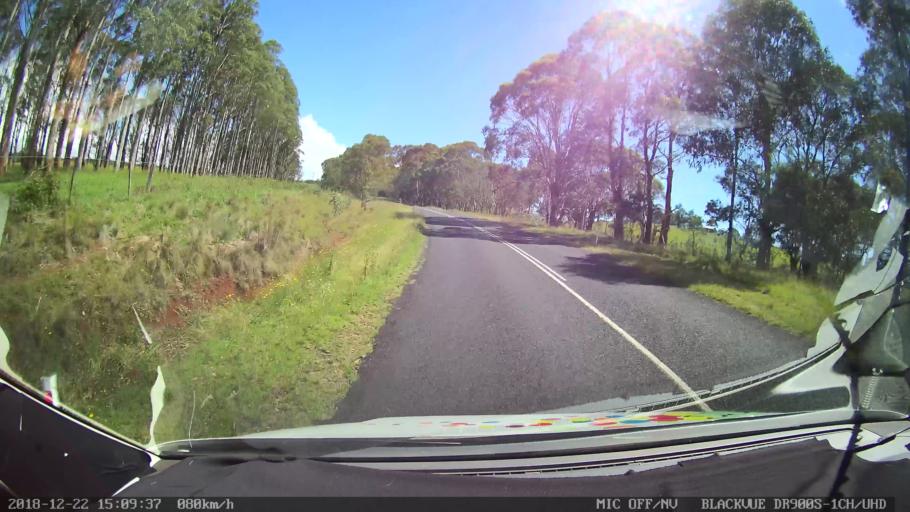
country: AU
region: New South Wales
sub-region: Bellingen
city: Dorrigo
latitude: -30.3256
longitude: 152.4070
